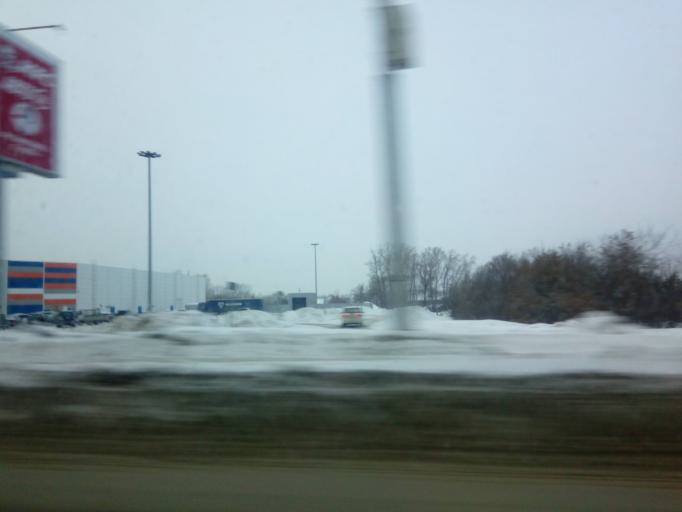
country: RU
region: Novosibirsk
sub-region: Novosibirskiy Rayon
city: Novosibirsk
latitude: 55.0116
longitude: 82.8773
